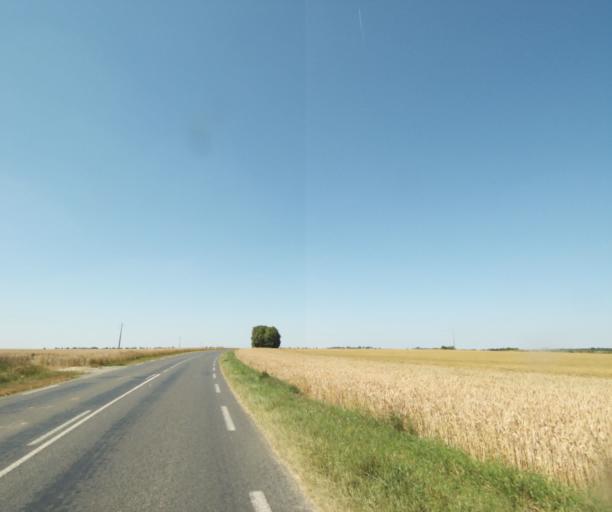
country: FR
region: Ile-de-France
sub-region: Departement de Seine-et-Marne
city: La Chapelle-la-Reine
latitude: 48.2965
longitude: 2.5743
